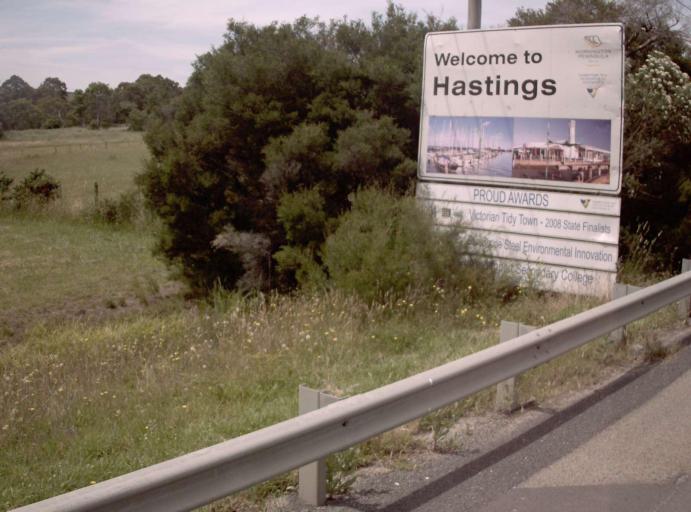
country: AU
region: Victoria
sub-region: Mornington Peninsula
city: Hastings
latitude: -38.2785
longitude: 145.1891
